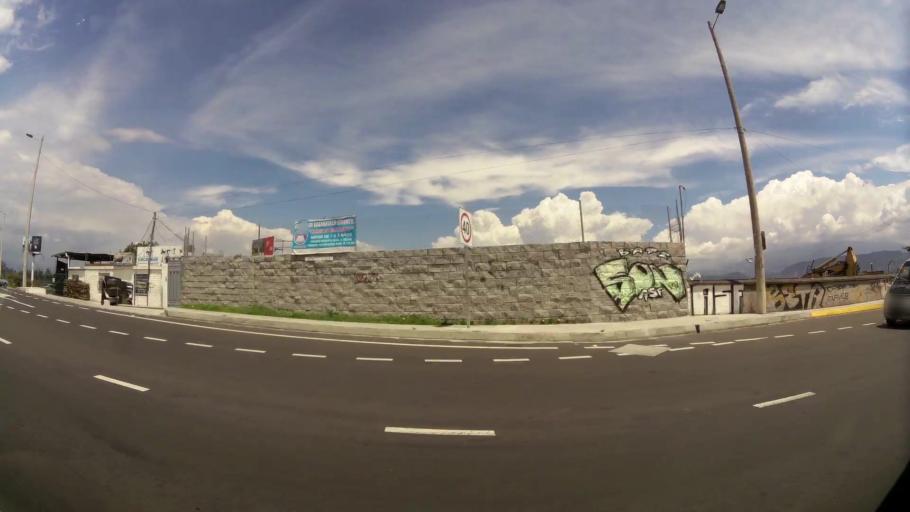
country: EC
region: Pichincha
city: Sangolqui
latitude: -0.2085
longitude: -78.3659
